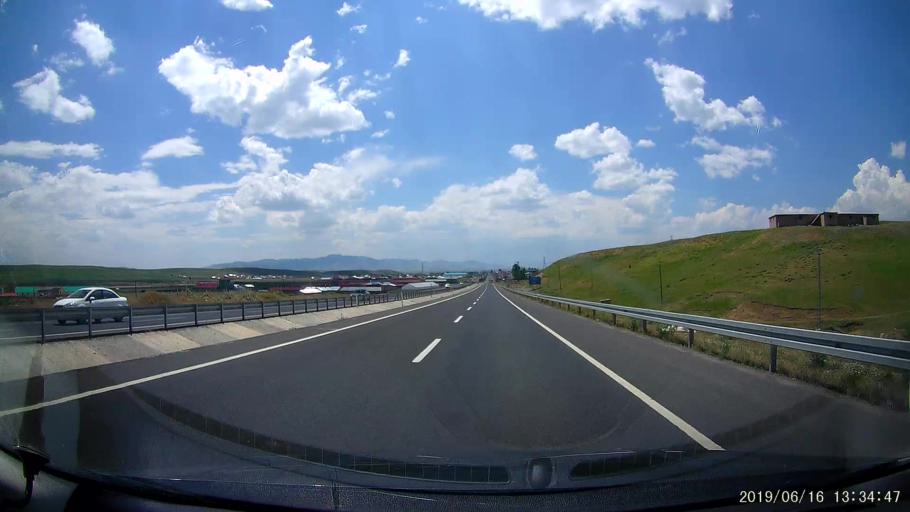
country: TR
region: Agri
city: Agri
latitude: 39.7129
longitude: 43.1177
